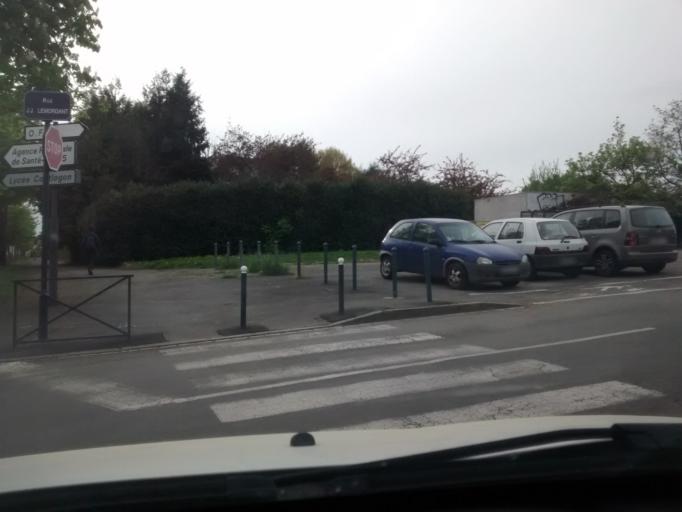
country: FR
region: Brittany
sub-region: Departement d'Ille-et-Vilaine
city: Rennes
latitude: 48.1228
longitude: -1.6886
